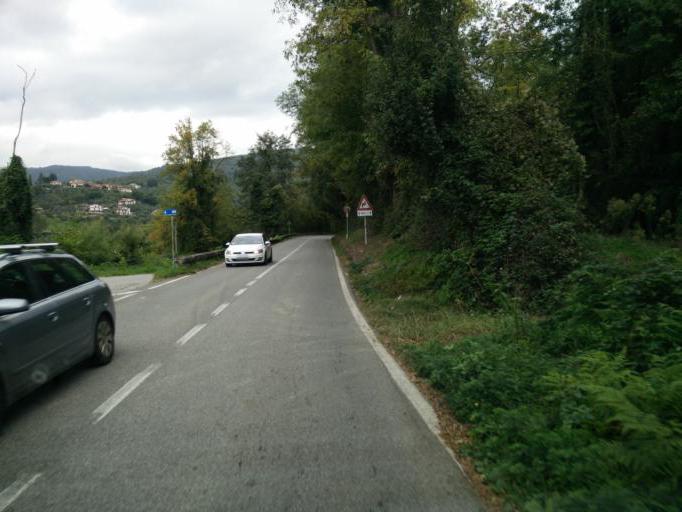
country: IT
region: Tuscany
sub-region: Provincia di Massa-Carrara
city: Fivizzano
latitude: 44.2164
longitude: 10.0932
